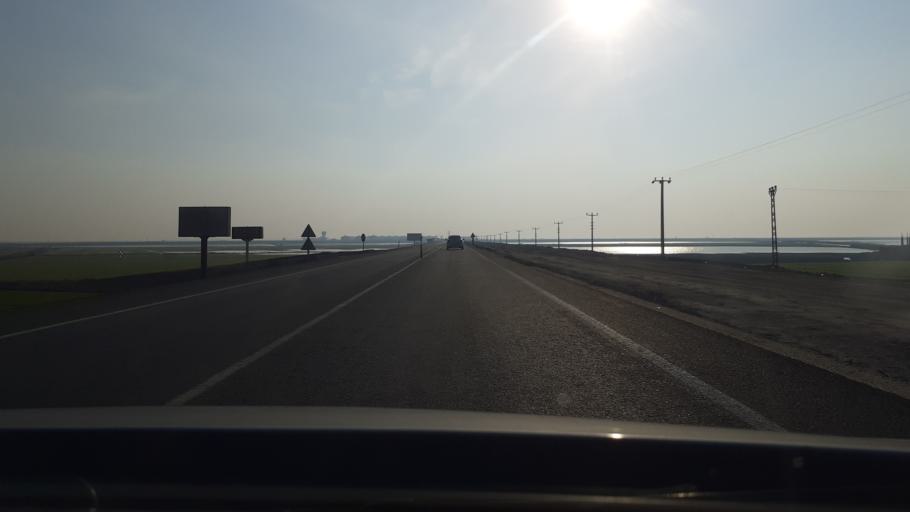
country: TR
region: Hatay
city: Serinyol
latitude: 36.3695
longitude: 36.2565
